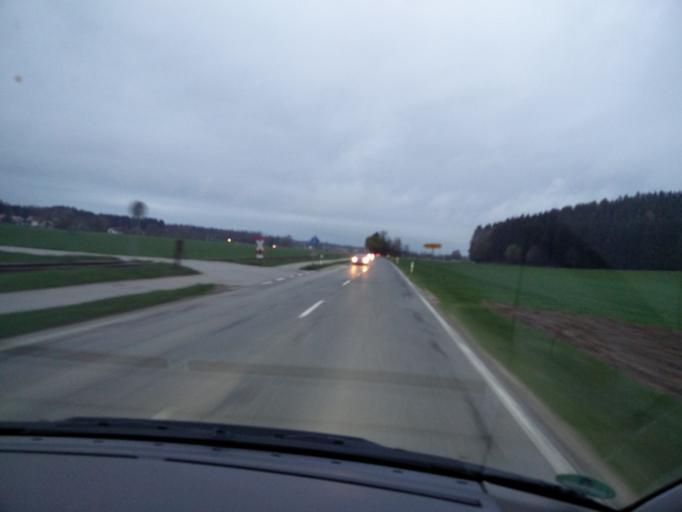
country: DE
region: Bavaria
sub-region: Upper Bavaria
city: Halfing
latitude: 47.9331
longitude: 12.2840
